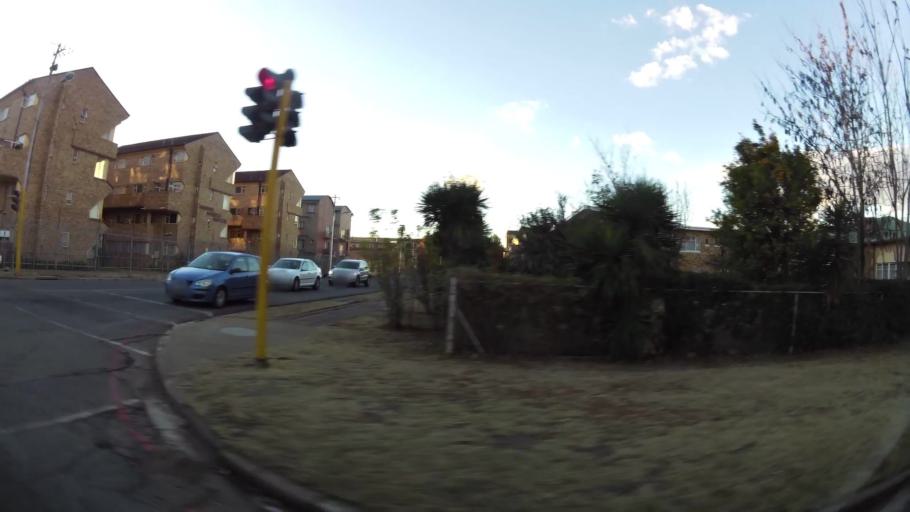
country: ZA
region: North-West
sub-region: Dr Kenneth Kaunda District Municipality
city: Potchefstroom
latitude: -26.7209
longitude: 27.0965
